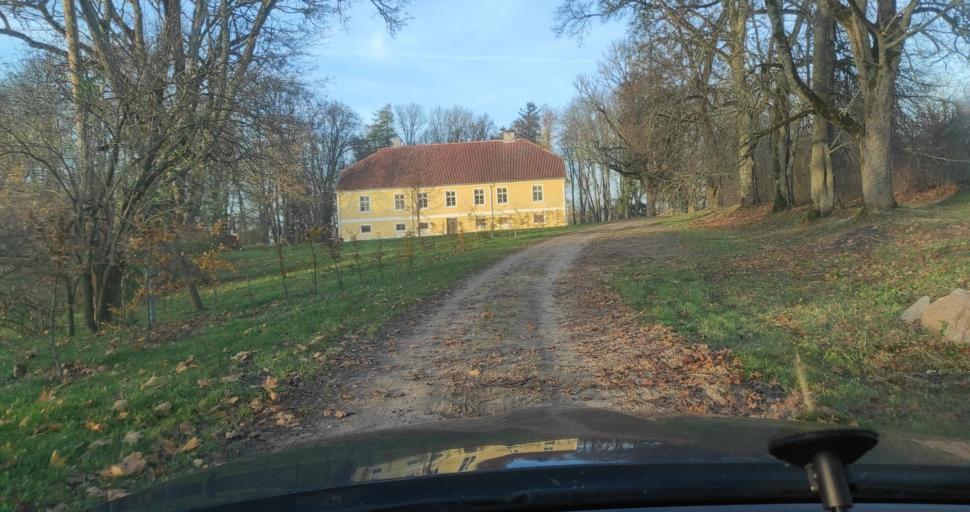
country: LV
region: Aizpute
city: Aizpute
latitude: 56.7512
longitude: 21.7972
